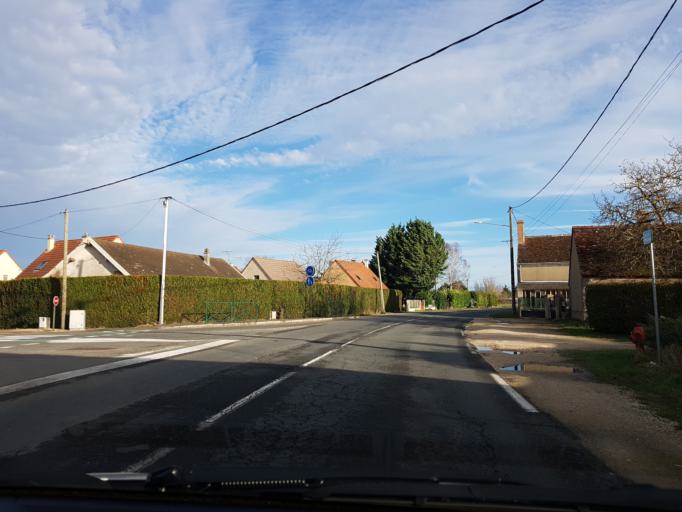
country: FR
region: Centre
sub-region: Departement du Loiret
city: Darvoy
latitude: 47.8545
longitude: 2.0852
